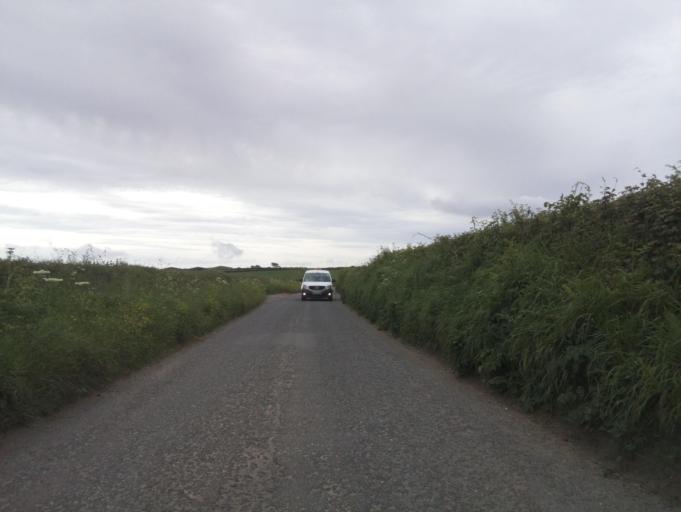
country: GB
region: England
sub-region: Devon
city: Dartmouth
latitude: 50.3246
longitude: -3.6393
